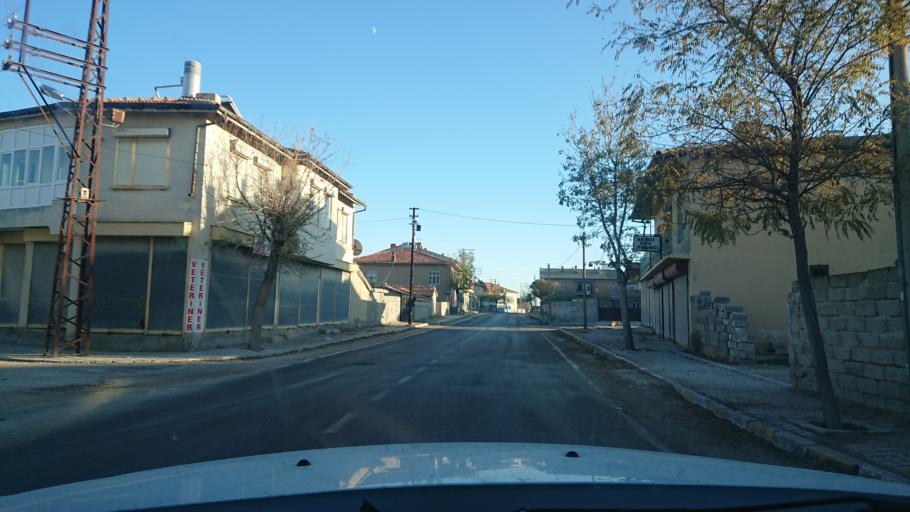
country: TR
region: Aksaray
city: Eskil
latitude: 38.5582
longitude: 33.1988
